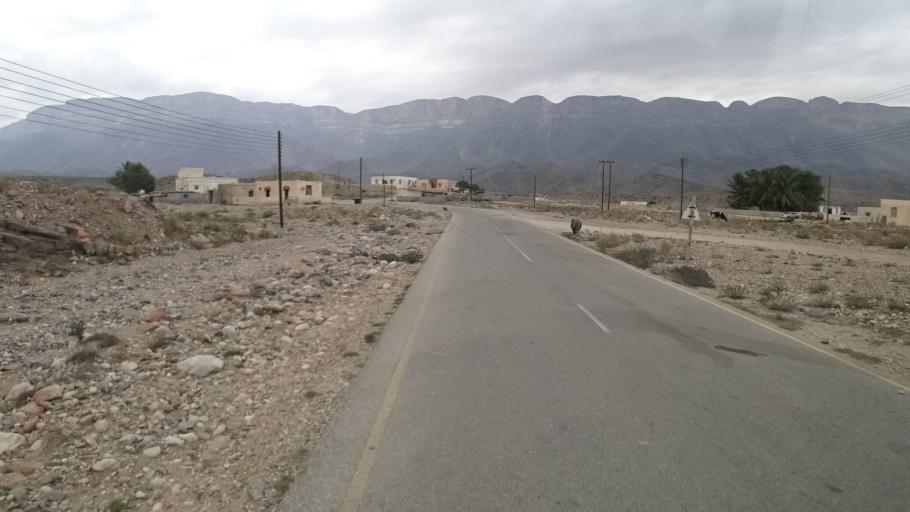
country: OM
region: Zufar
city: Salalah
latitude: 17.1652
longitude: 54.9812
